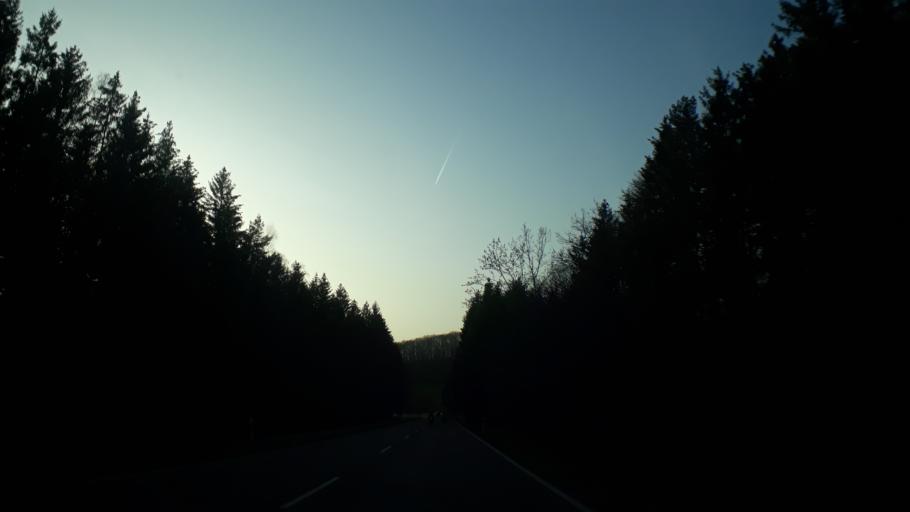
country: DE
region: Rheinland-Pfalz
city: Hummel
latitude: 50.5048
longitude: 6.8147
